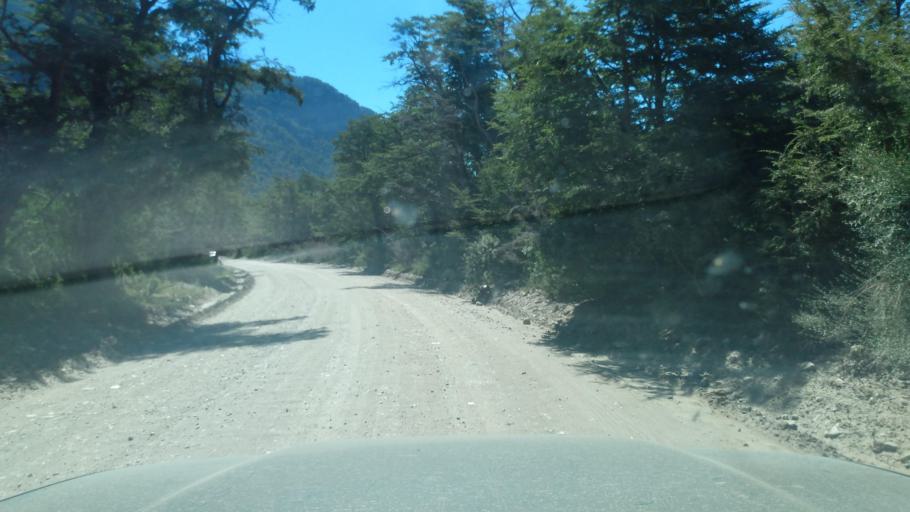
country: AR
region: Neuquen
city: Villa La Angostura
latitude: -40.6211
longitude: -71.5963
